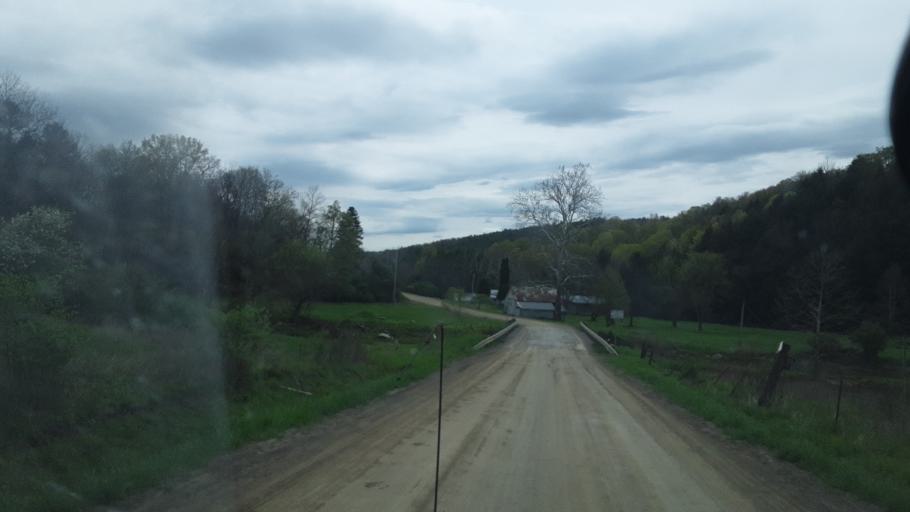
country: US
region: New York
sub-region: Steuben County
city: Addison
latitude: 42.0997
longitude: -77.3364
